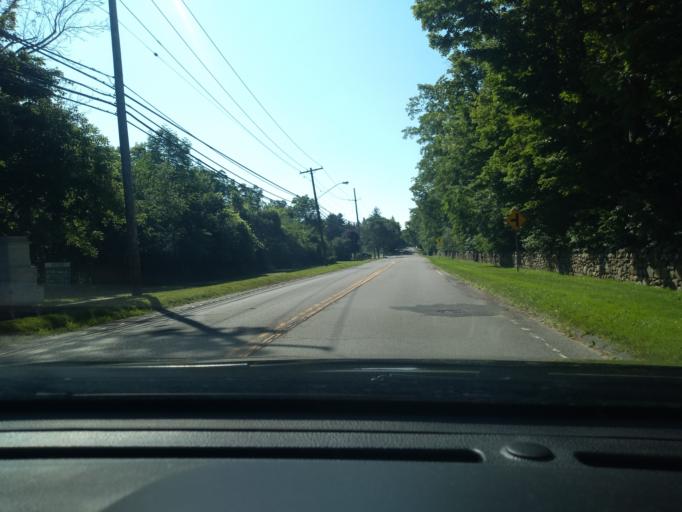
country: US
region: New York
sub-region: Erie County
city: Billington Heights
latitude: 42.7728
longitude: -78.6350
